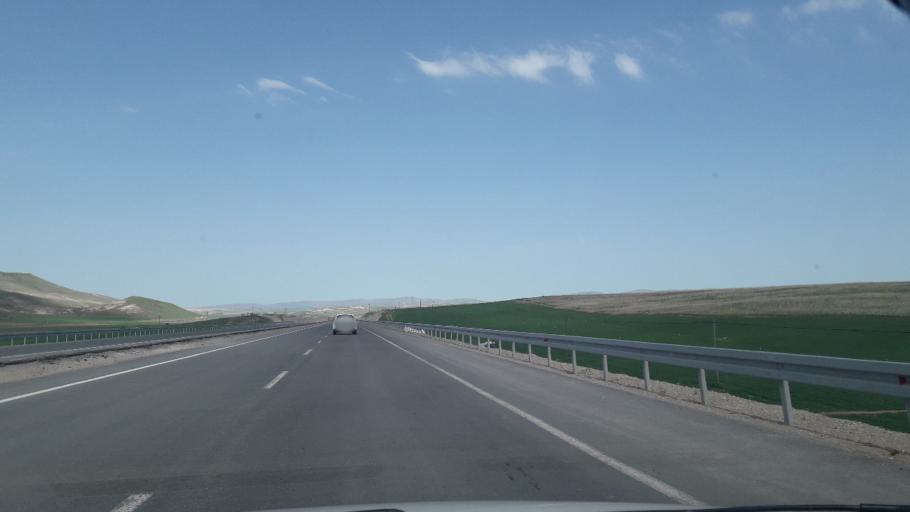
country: TR
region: Sivas
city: Deliktas
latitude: 39.2045
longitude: 37.2182
